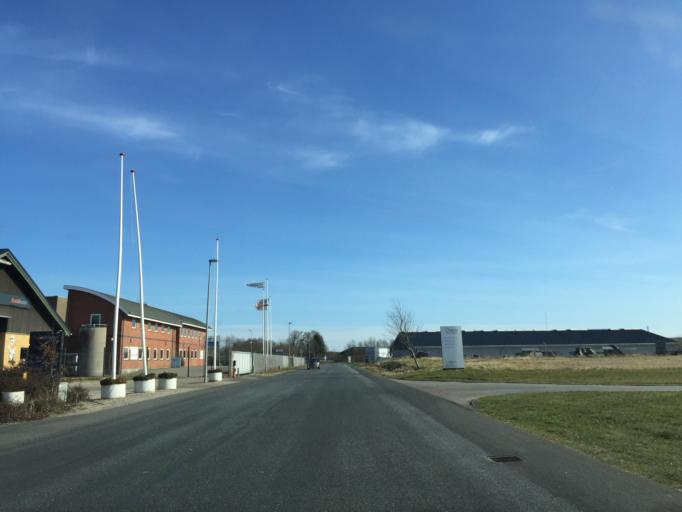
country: DK
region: Central Jutland
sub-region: Silkeborg Kommune
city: Silkeborg
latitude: 56.2045
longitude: 9.5677
